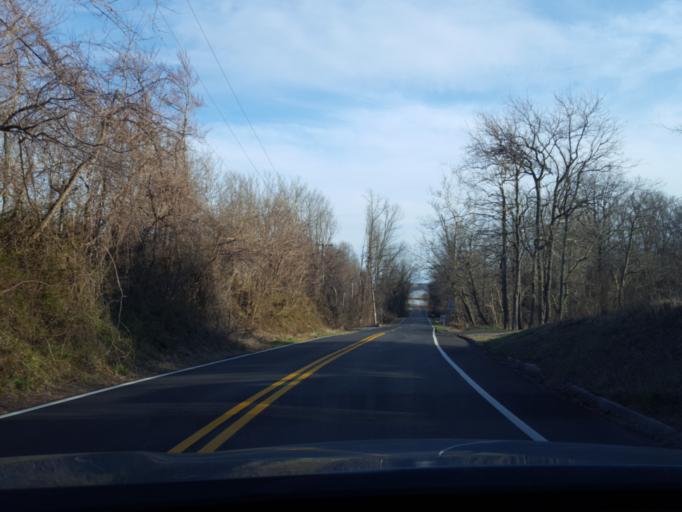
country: US
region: Maryland
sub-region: Anne Arundel County
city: Deale
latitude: 38.7549
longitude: -76.5603
